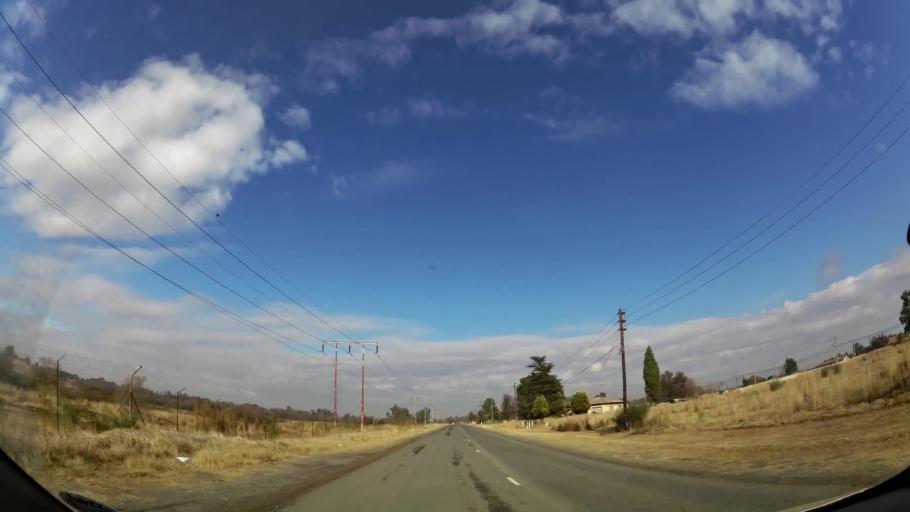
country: ZA
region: Gauteng
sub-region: Sedibeng District Municipality
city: Meyerton
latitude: -26.5169
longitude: 28.0491
